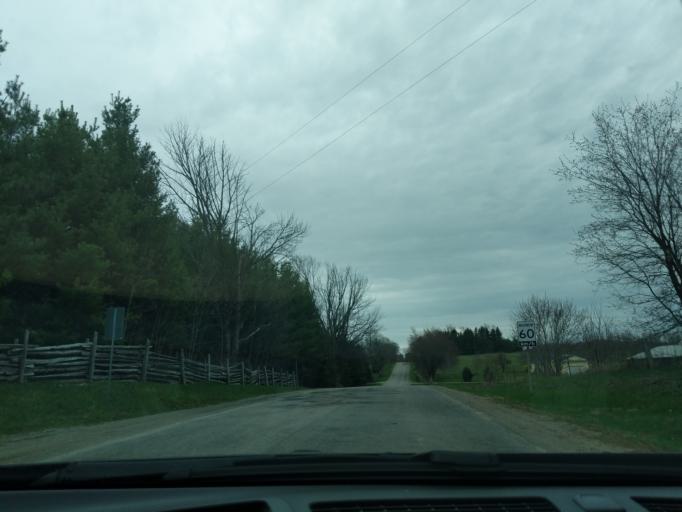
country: CA
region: Ontario
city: Orangeville
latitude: 44.0147
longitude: -79.9673
